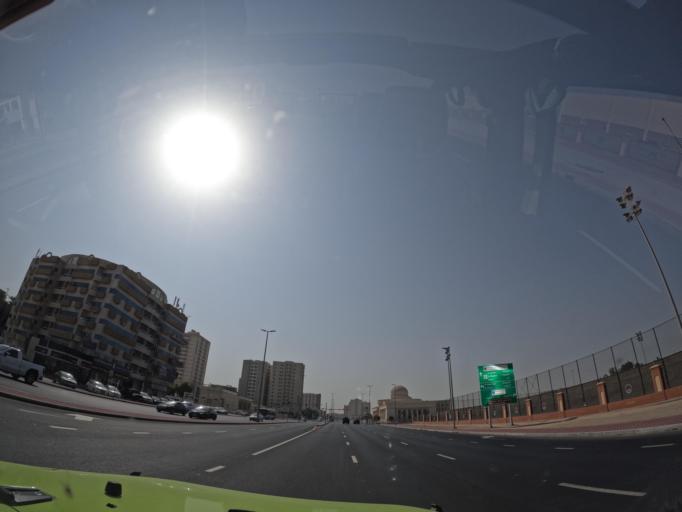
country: AE
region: Ajman
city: Ajman
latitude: 25.4106
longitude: 55.5094
